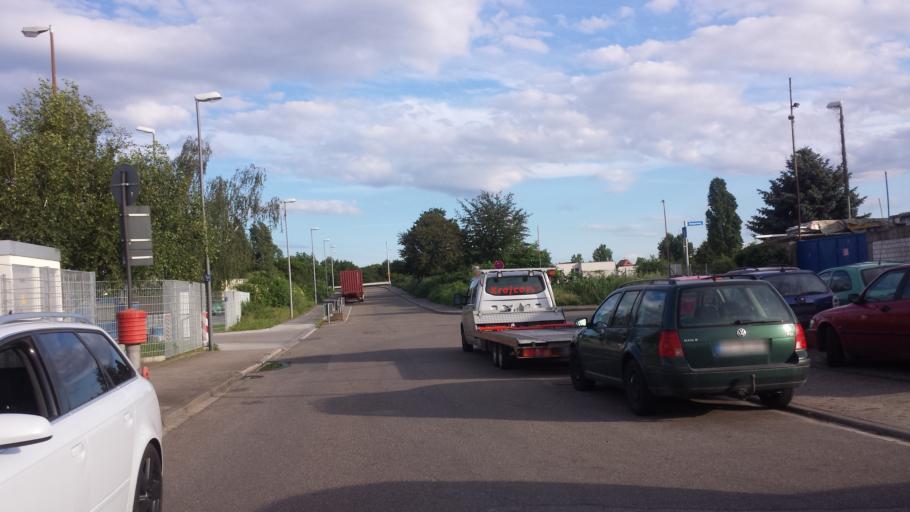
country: DE
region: Rheinland-Pfalz
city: Gartenstadt
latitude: 49.4522
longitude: 8.4172
